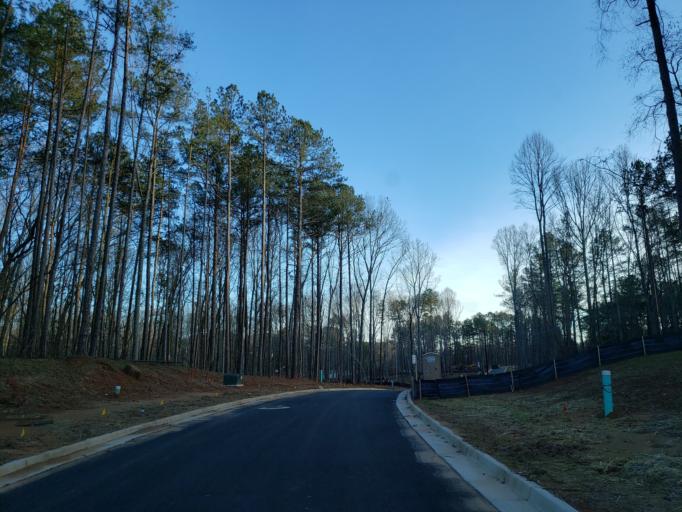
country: US
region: Georgia
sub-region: Cobb County
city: Acworth
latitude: 34.0296
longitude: -84.7312
